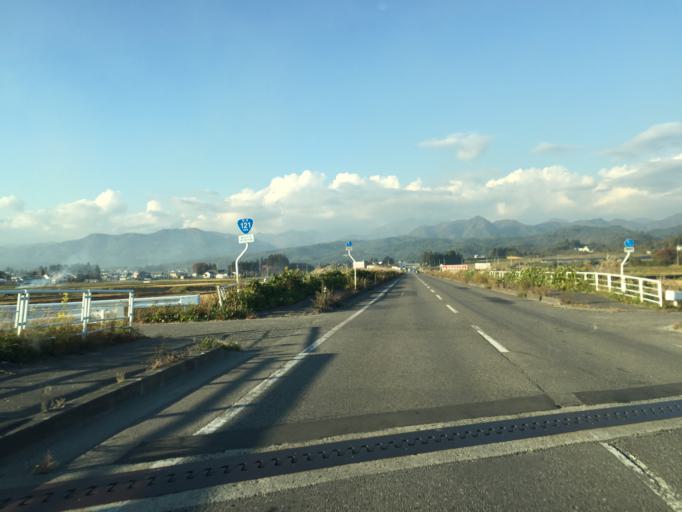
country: JP
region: Fukushima
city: Kitakata
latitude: 37.6776
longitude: 139.8880
